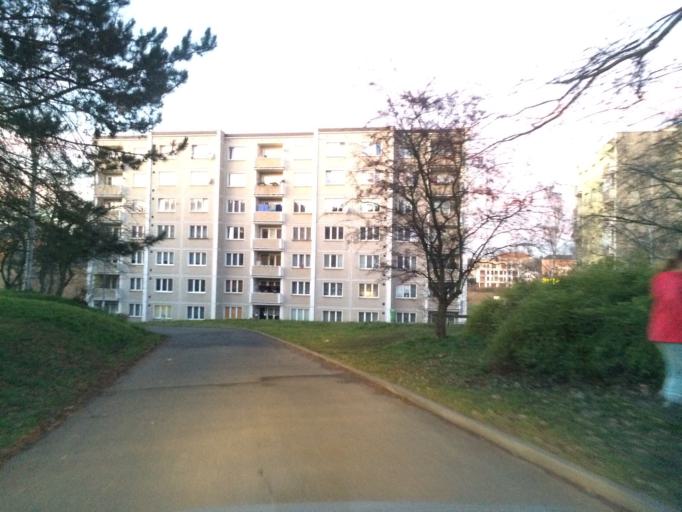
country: CZ
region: Central Bohemia
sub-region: Okres Kladno
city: Slany
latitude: 50.2284
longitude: 14.0712
